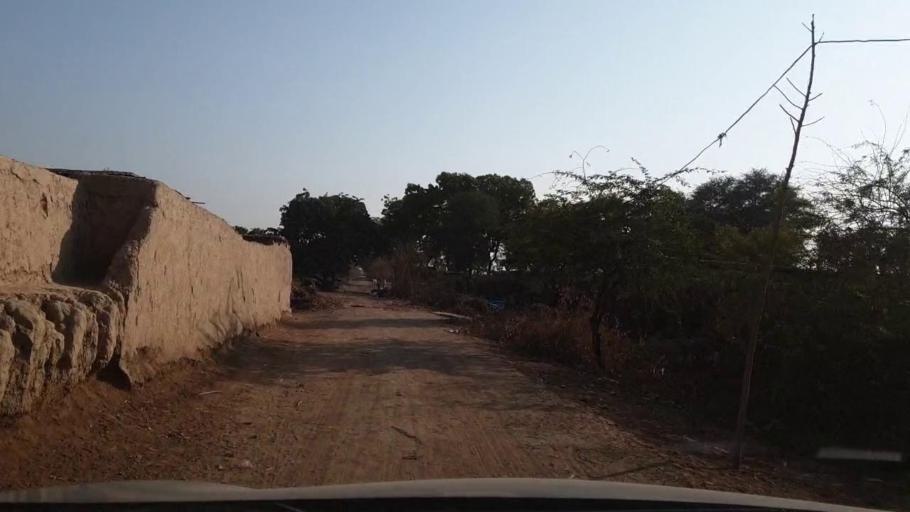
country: PK
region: Sindh
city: Tando Allahyar
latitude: 25.5738
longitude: 68.7736
